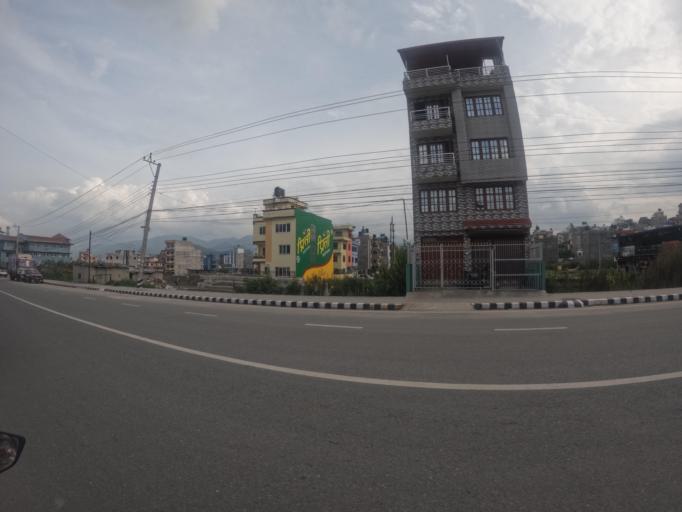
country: NP
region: Central Region
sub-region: Bagmati Zone
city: Bhaktapur
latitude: 27.6804
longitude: 85.3972
